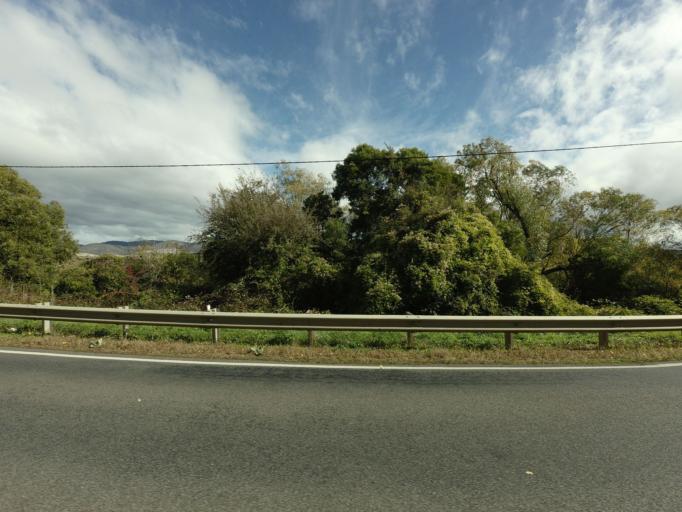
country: AU
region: Tasmania
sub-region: Derwent Valley
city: New Norfolk
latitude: -42.7410
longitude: 146.9832
